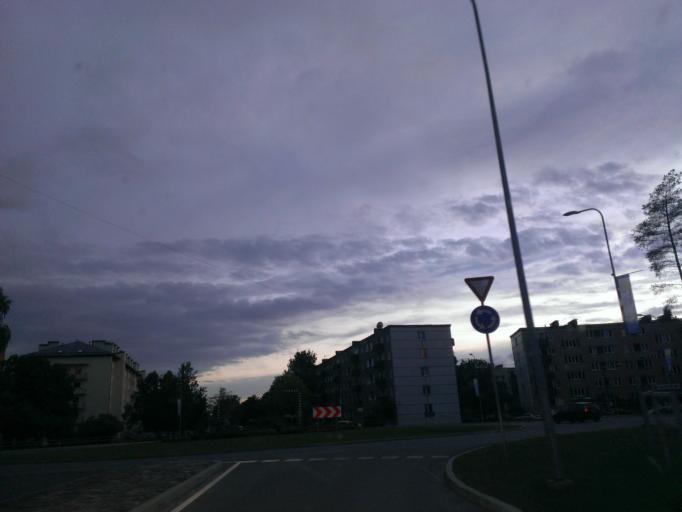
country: LV
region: Ogre
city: Ogre
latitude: 56.8245
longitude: 24.5997
